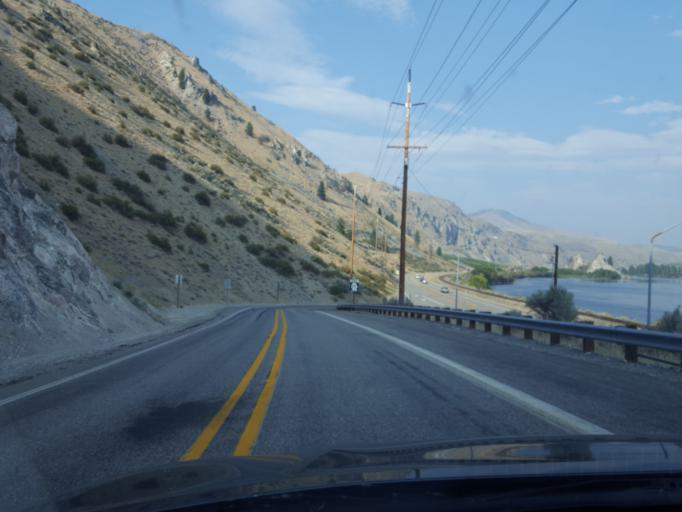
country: US
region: Washington
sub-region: Chelan County
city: Entiat
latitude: 47.7675
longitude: -120.1766
